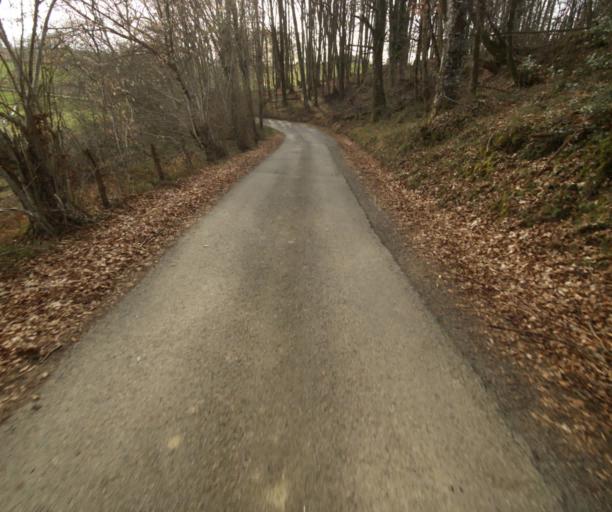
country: FR
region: Limousin
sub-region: Departement de la Correze
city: Chamboulive
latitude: 45.4377
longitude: 1.7428
